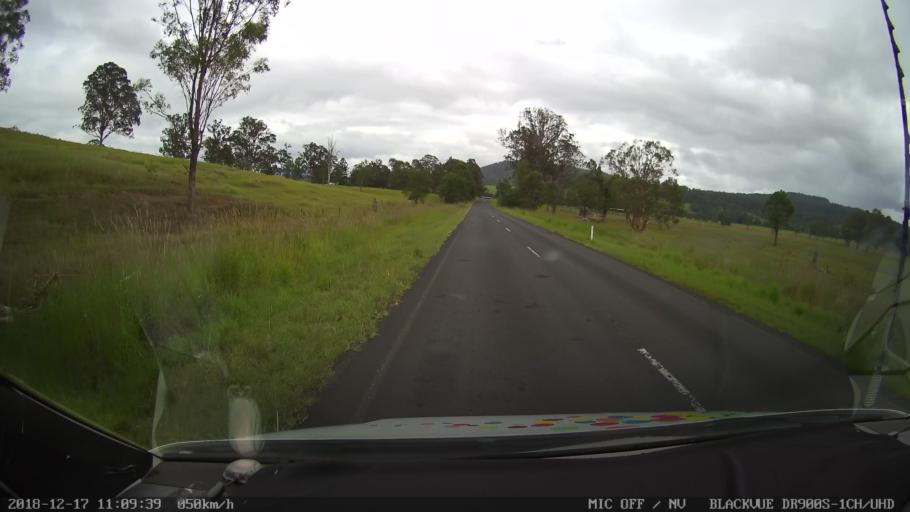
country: AU
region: New South Wales
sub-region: Kyogle
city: Kyogle
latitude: -28.7529
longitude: 152.6534
